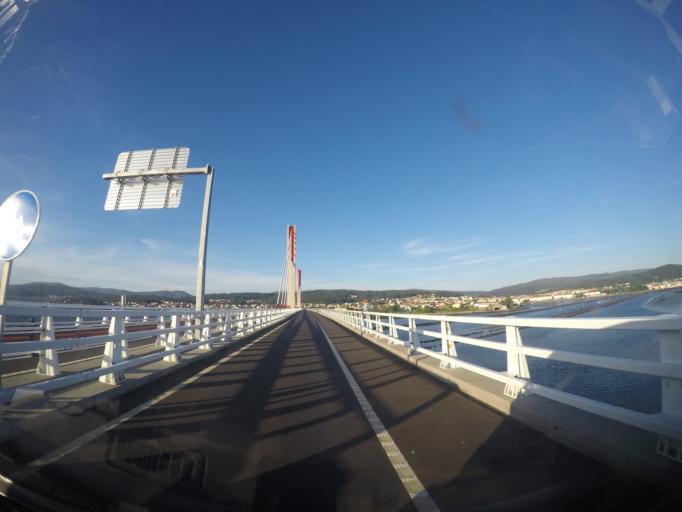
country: ES
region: Galicia
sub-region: Provincia da Coruna
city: Noia
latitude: 42.7917
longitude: -8.9046
